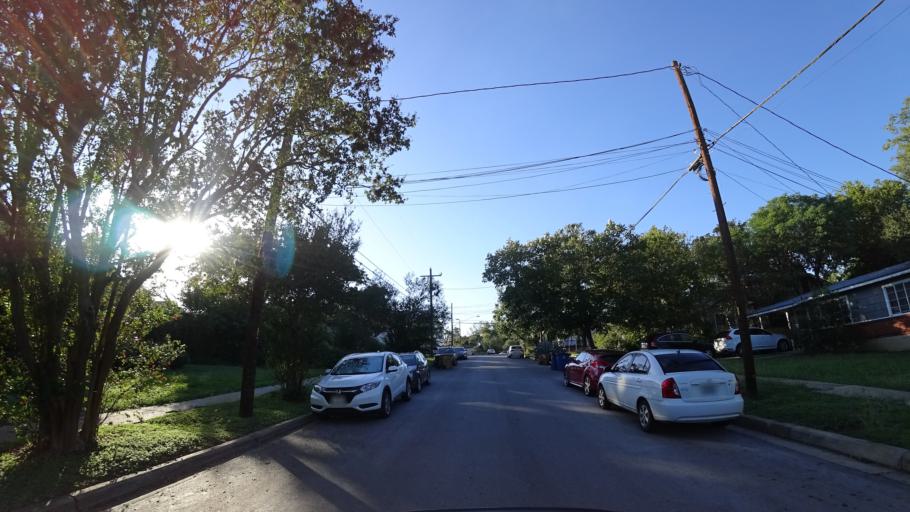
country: US
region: Texas
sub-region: Travis County
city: Austin
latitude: 30.2968
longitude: -97.7345
